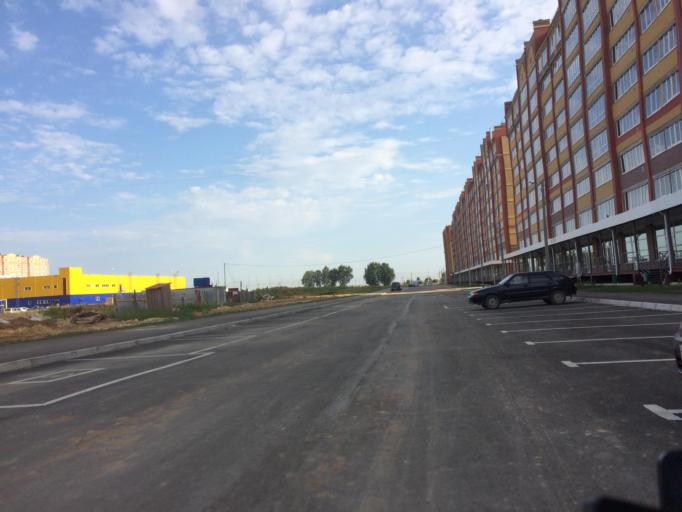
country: RU
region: Mariy-El
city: Medvedevo
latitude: 56.6358
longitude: 47.8195
